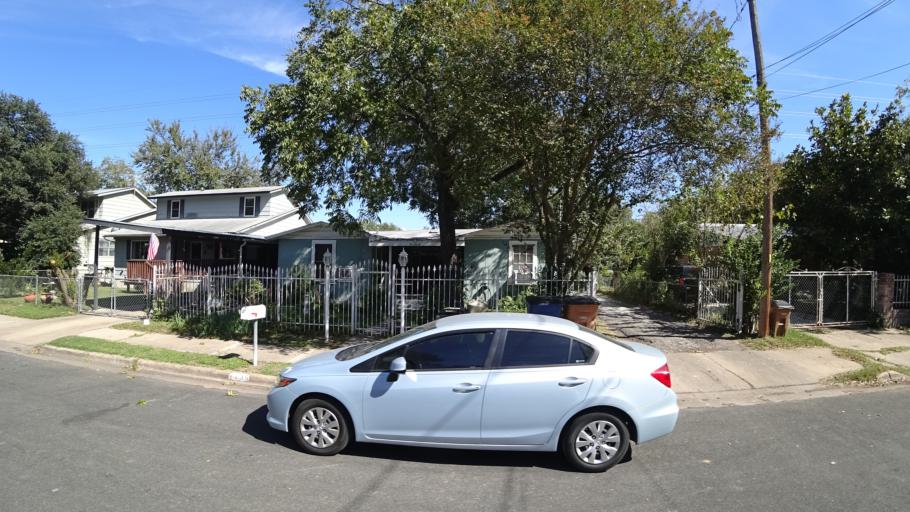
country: US
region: Texas
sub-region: Travis County
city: Austin
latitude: 30.2704
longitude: -97.6867
